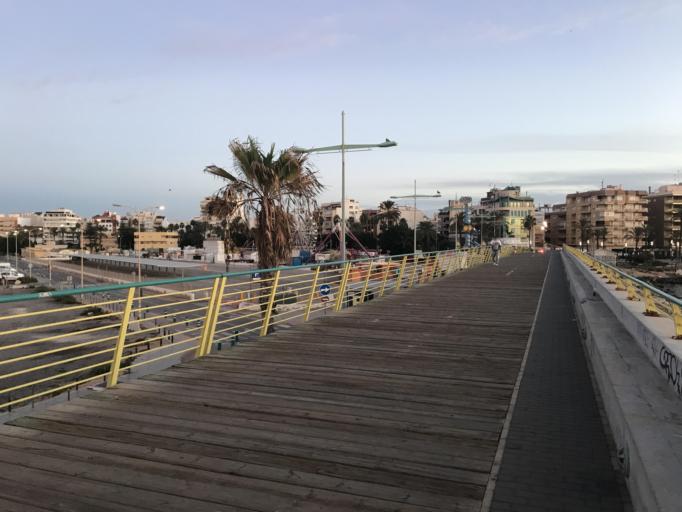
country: ES
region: Valencia
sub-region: Provincia de Alicante
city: Torrevieja
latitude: 37.9726
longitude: -0.6788
